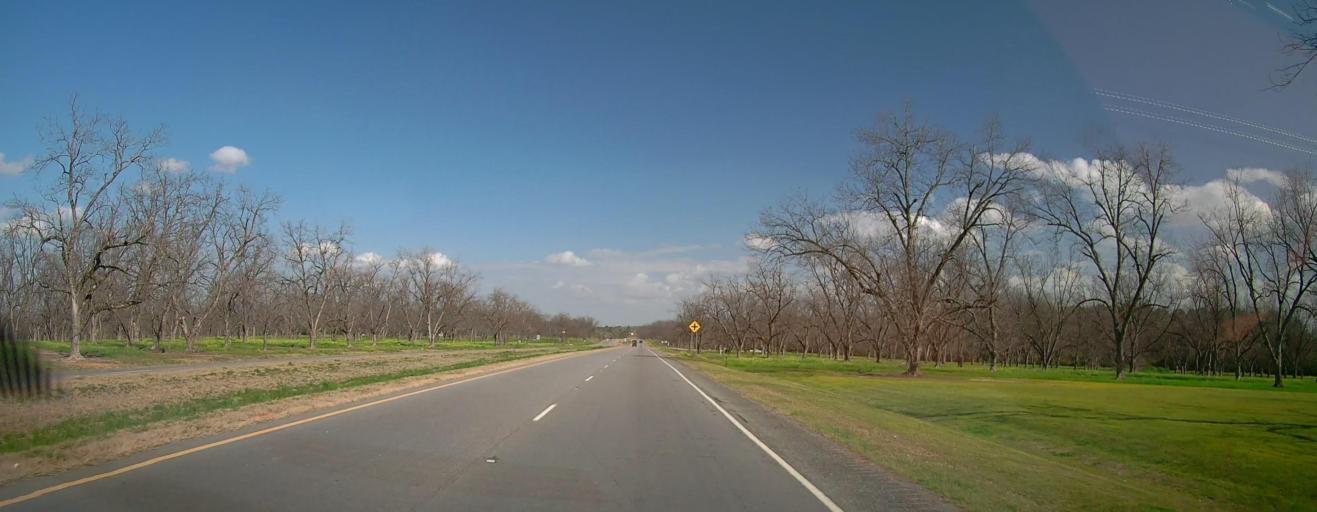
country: US
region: Georgia
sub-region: Dodge County
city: Eastman
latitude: 32.1989
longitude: -83.2316
